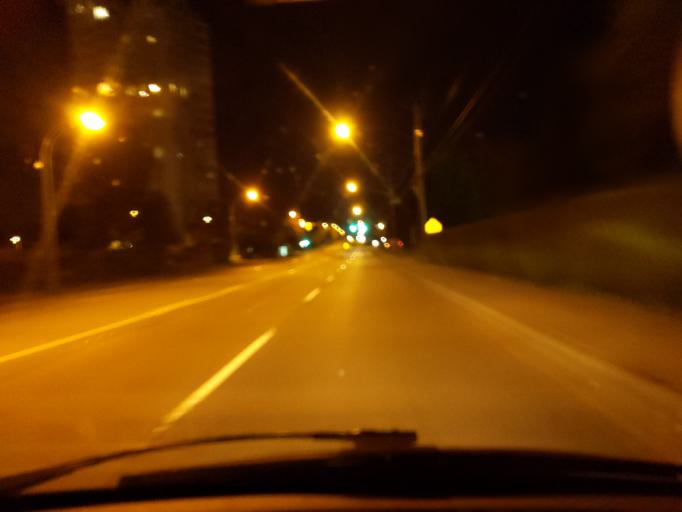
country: CA
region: British Columbia
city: Surrey
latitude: 49.1916
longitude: -122.8102
